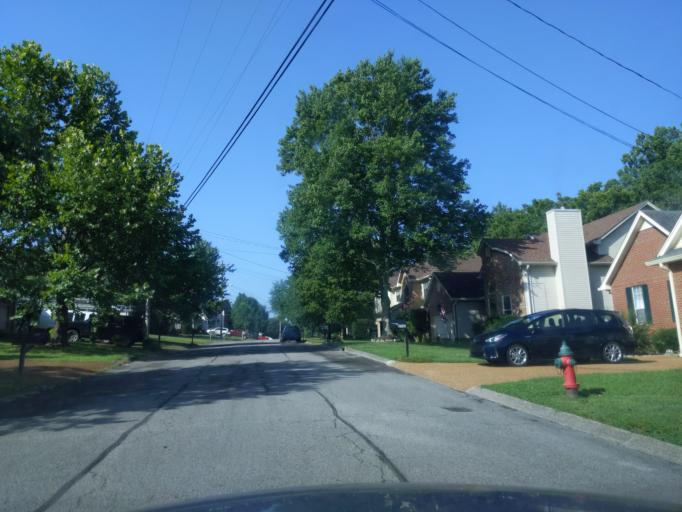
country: US
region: Tennessee
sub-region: Williamson County
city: Brentwood Estates
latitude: 36.0237
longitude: -86.7207
